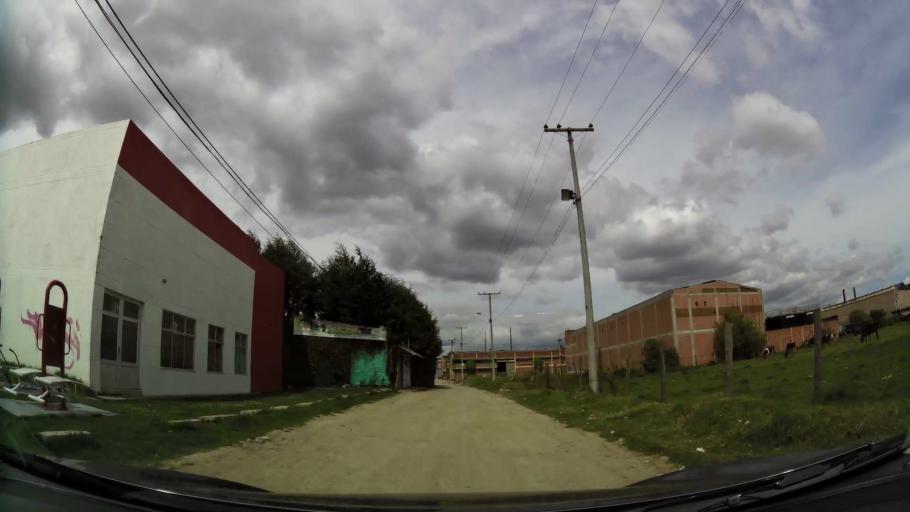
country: CO
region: Cundinamarca
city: Funza
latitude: 4.7053
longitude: -74.2013
